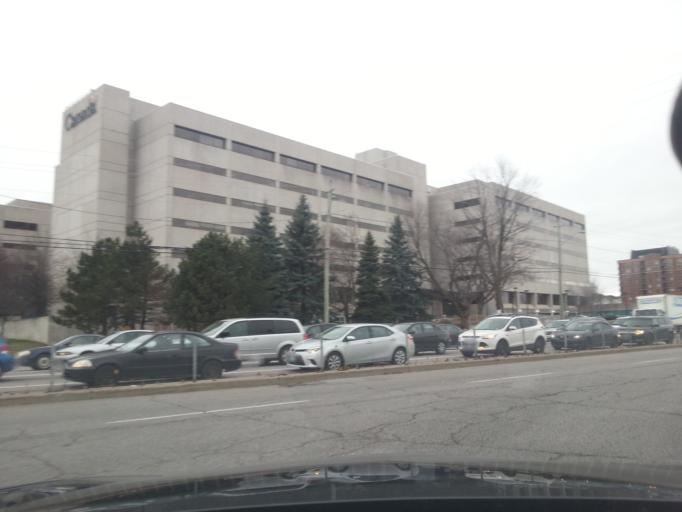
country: CA
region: Ontario
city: Ottawa
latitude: 45.3656
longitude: -75.7306
